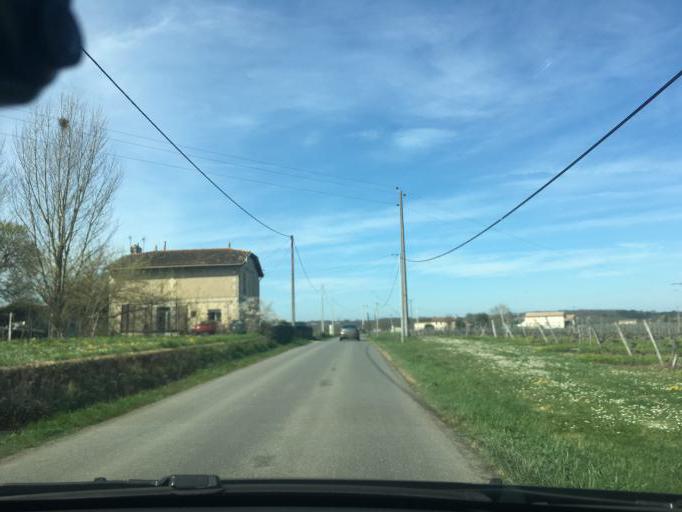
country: FR
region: Aquitaine
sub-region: Departement de la Gironde
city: Saint-Germain-du-Puch
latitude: 44.8476
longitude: -0.3456
